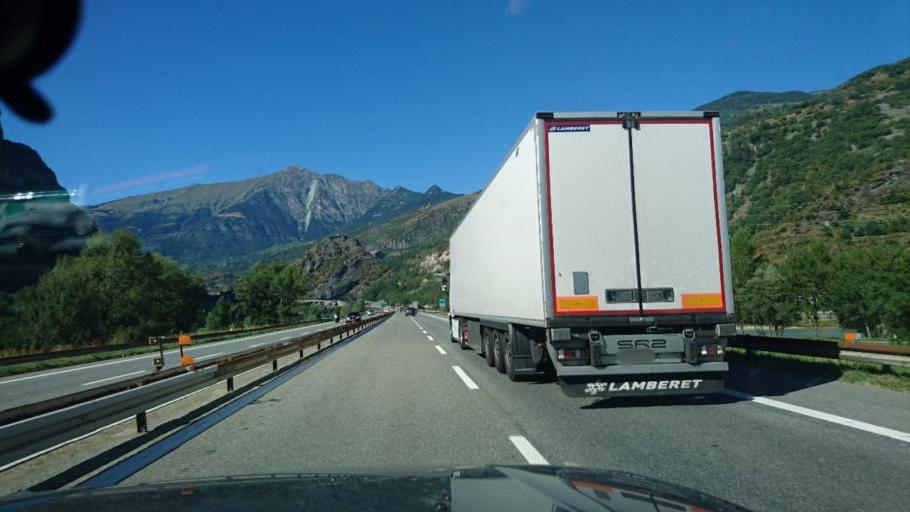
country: IT
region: Aosta Valley
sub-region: Valle d'Aosta
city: Montjovet
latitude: 45.7086
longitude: 7.6693
